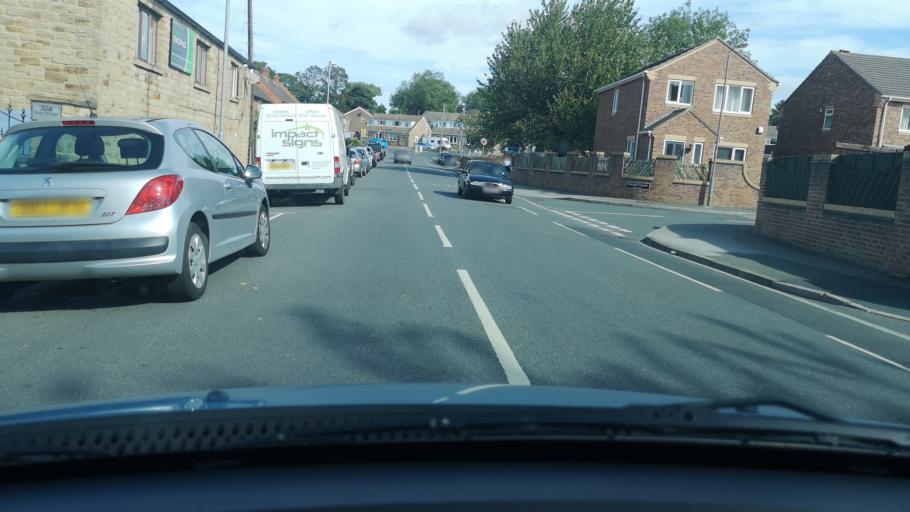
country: GB
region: England
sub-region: City and Borough of Wakefield
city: Ossett
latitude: 53.6697
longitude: -1.5754
